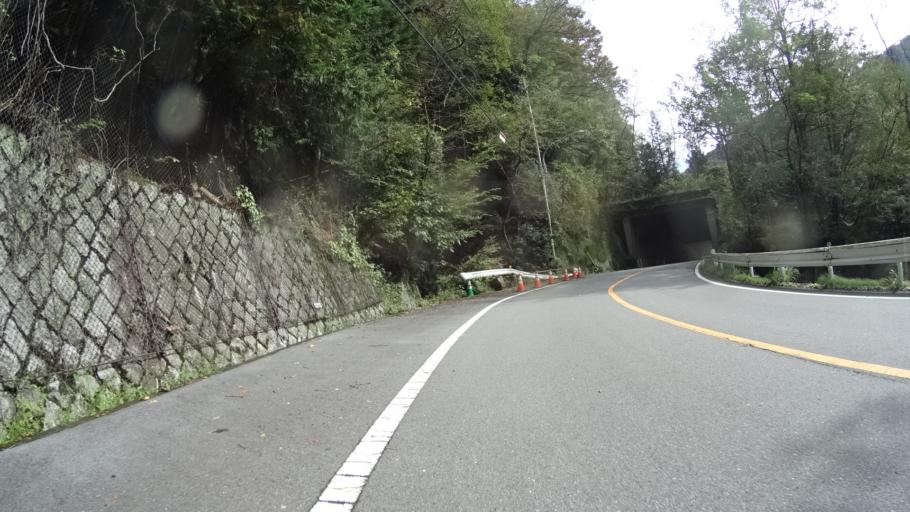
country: JP
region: Yamanashi
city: Otsuki
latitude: 35.7871
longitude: 138.9517
